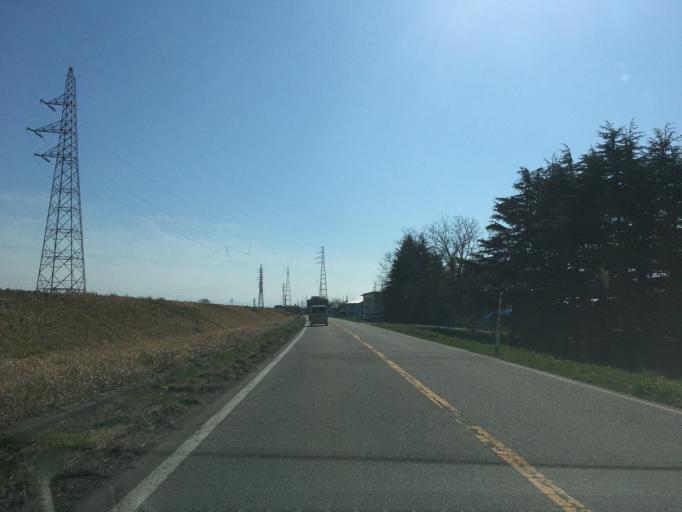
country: JP
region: Toyama
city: Nishishinminato
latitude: 36.7833
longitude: 137.0619
